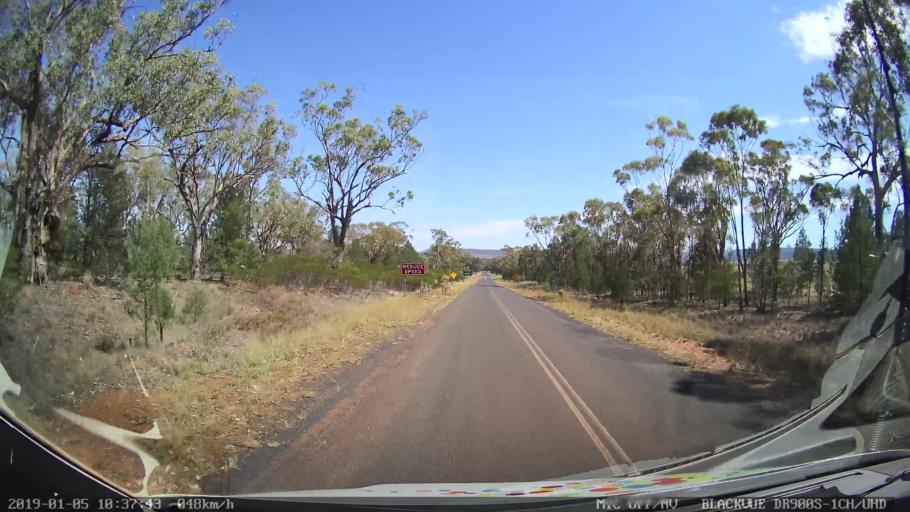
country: AU
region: New South Wales
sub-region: Gilgandra
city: Gilgandra
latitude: -31.4727
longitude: 148.9208
